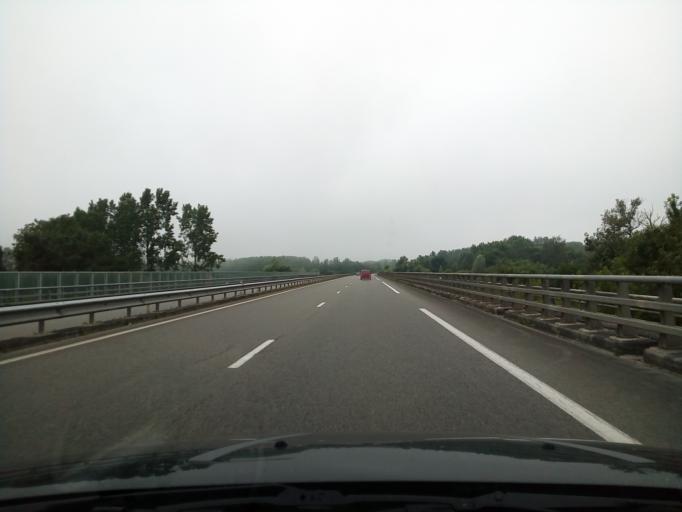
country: FR
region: Poitou-Charentes
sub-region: Departement de la Charente
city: Jarnac
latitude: 45.6723
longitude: -0.1607
